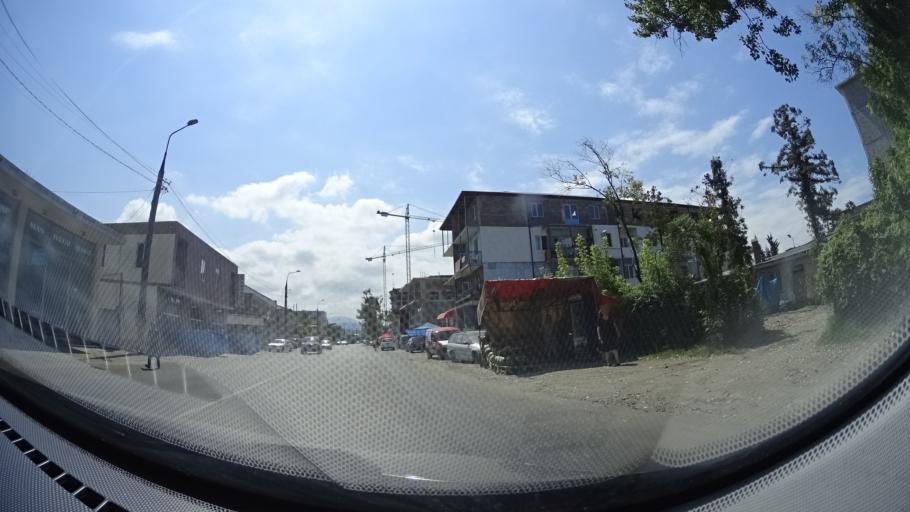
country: GE
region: Ajaria
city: Batumi
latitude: 41.6237
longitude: 41.6131
